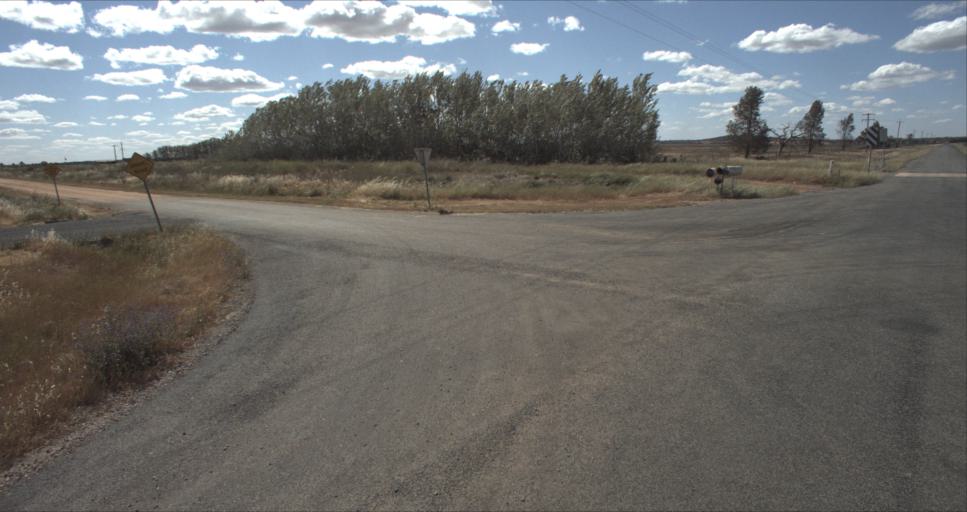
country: AU
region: New South Wales
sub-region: Leeton
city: Leeton
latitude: -34.4595
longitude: 146.2530
